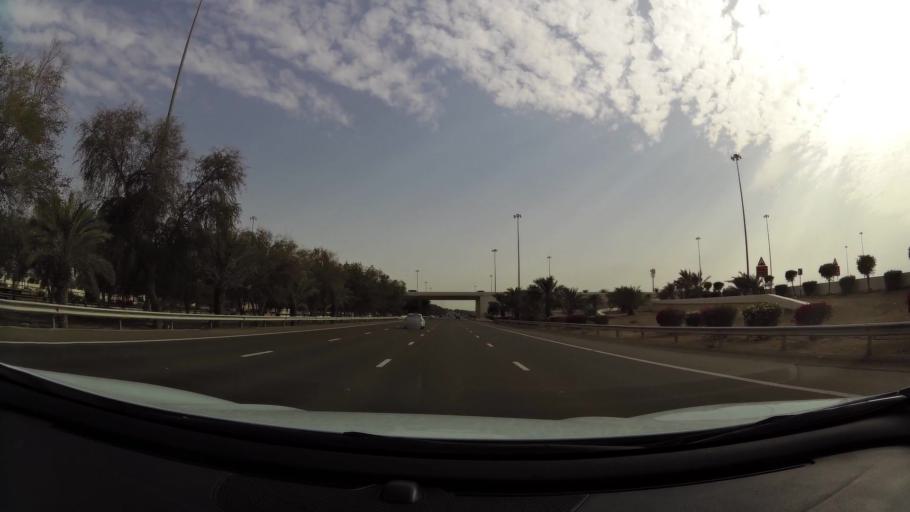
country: AE
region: Abu Dhabi
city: Abu Dhabi
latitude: 24.4656
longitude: 54.6769
